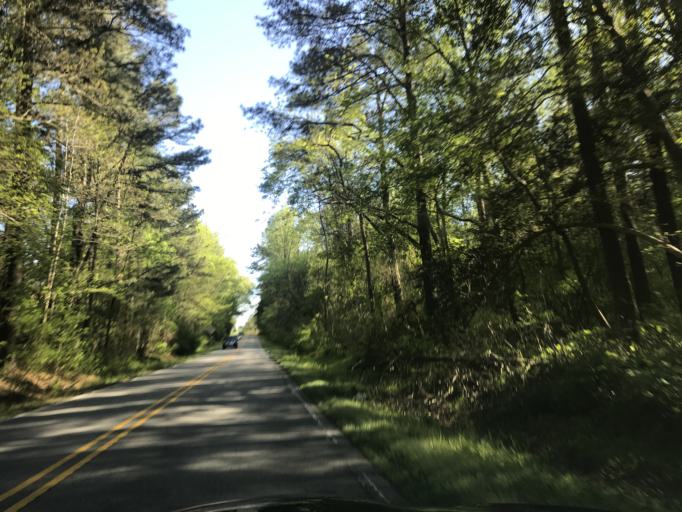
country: US
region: North Carolina
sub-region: Wake County
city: Knightdale
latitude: 35.8236
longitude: -78.5554
